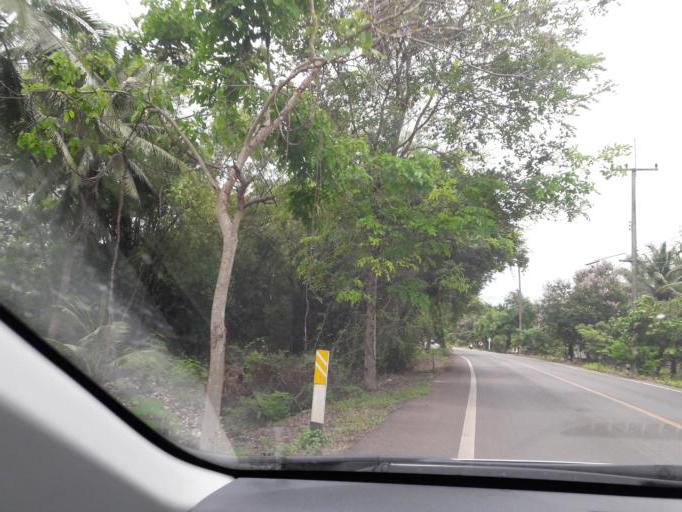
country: TH
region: Samut Sakhon
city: Ban Phaeo
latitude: 13.6160
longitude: 100.0228
